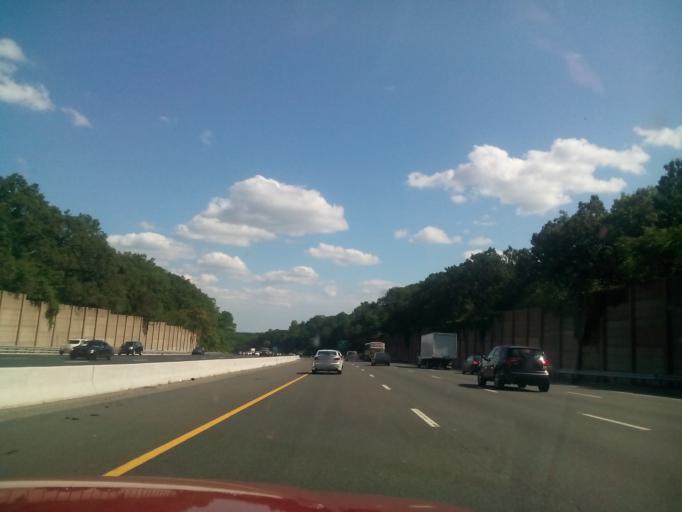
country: US
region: New Jersey
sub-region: Morris County
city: Mountain Lakes
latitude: 40.8725
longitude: -74.4639
